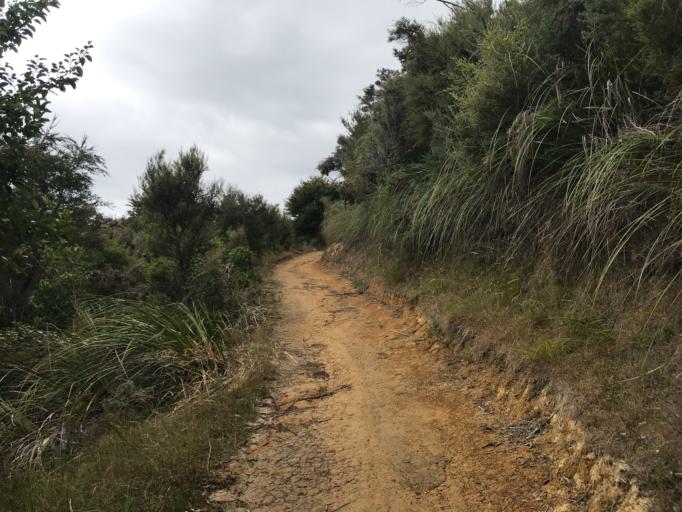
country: NZ
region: Marlborough
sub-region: Marlborough District
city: Picton
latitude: -41.2276
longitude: 173.9591
